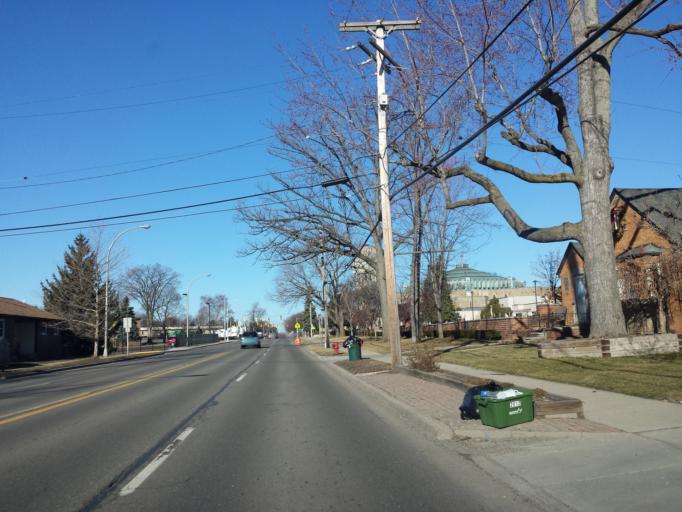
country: US
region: Michigan
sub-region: Oakland County
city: Berkley
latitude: 42.5037
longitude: -83.1687
